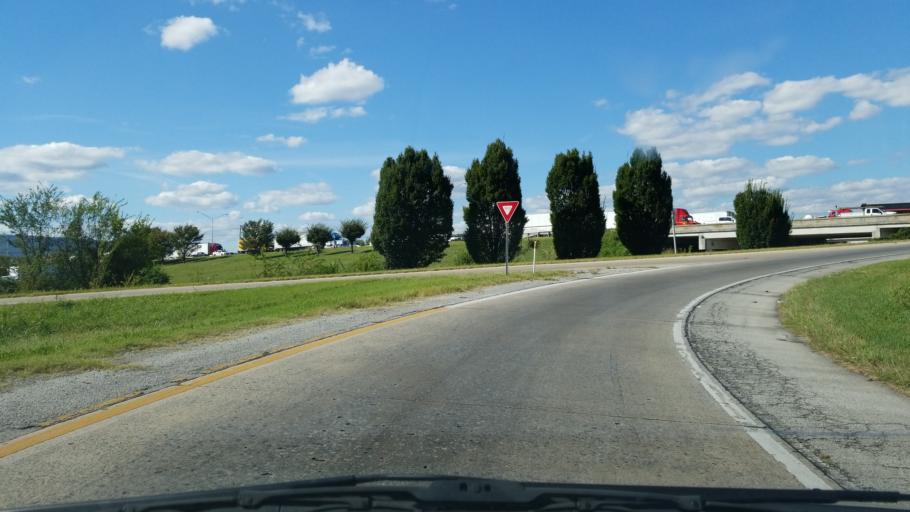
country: US
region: Tennessee
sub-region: Hamilton County
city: Chattanooga
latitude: 35.0283
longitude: -85.3115
